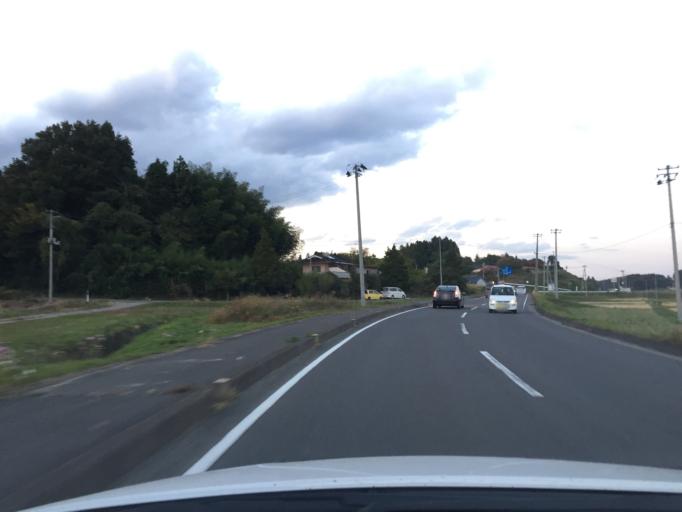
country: JP
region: Fukushima
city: Motomiya
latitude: 37.4910
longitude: 140.4519
